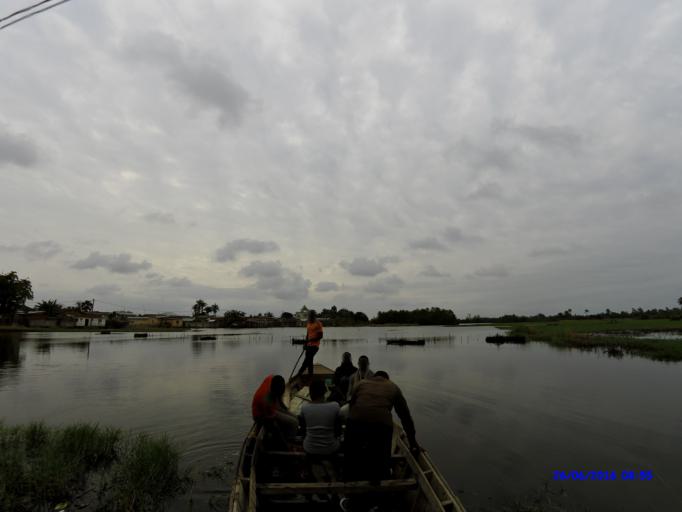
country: BJ
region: Atlantique
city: Hevie
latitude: 6.3532
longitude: 2.3071
